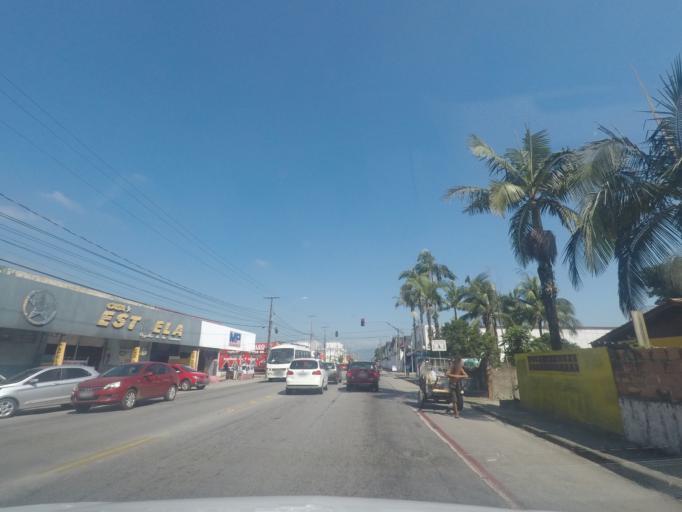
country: BR
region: Parana
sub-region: Paranagua
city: Paranagua
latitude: -25.5438
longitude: -48.5390
